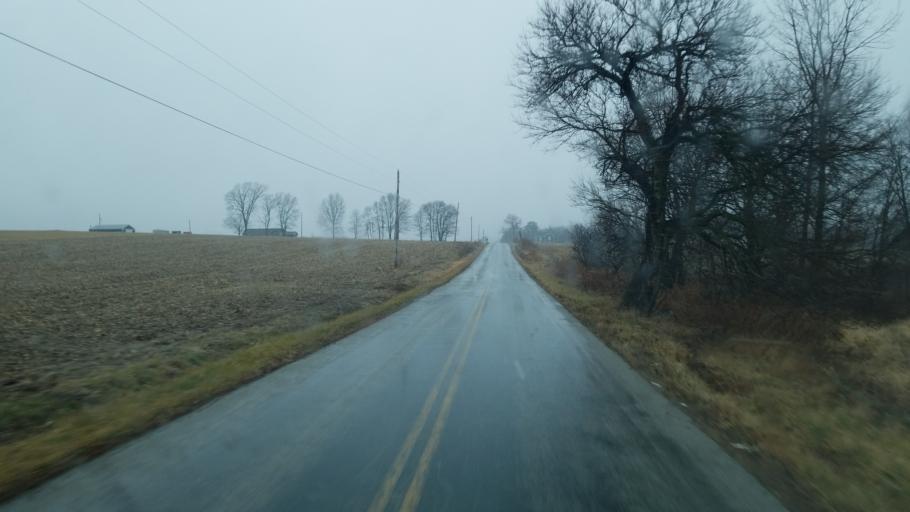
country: US
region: Ohio
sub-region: Licking County
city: Utica
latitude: 40.2090
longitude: -82.3372
